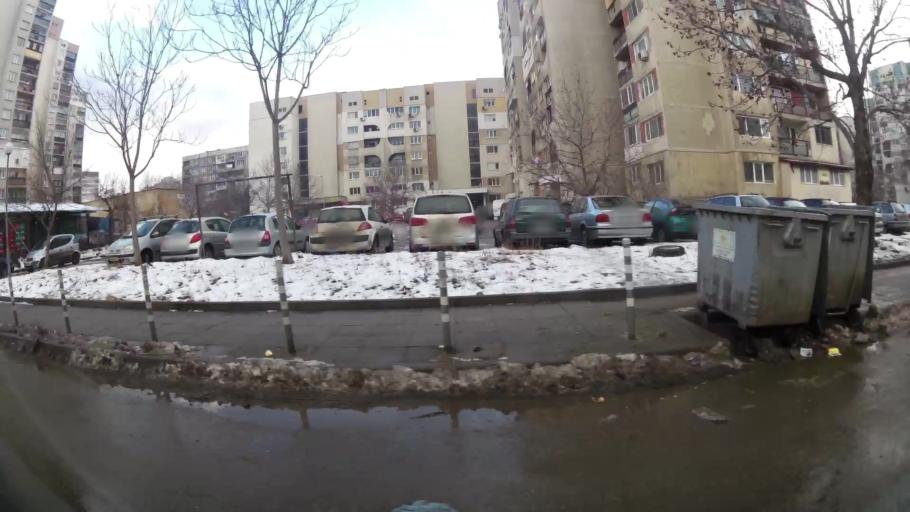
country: BG
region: Sofia-Capital
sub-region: Stolichna Obshtina
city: Sofia
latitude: 42.6980
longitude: 23.2863
